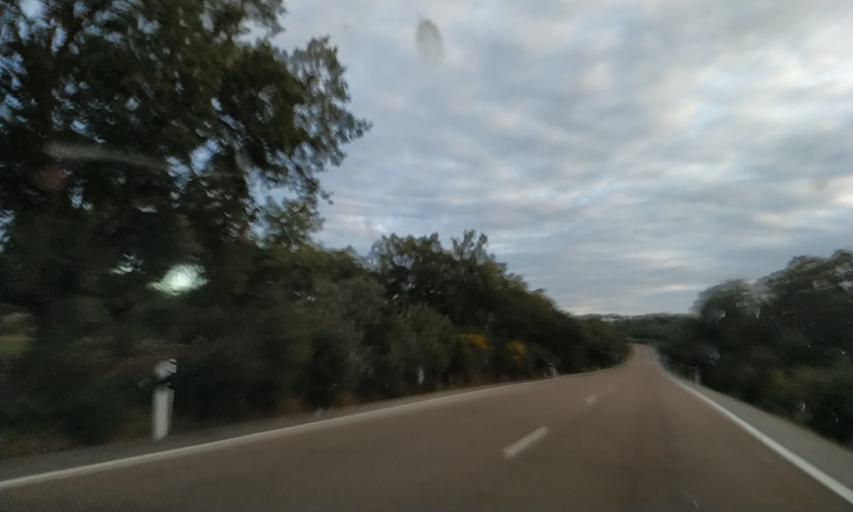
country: ES
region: Extremadura
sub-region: Provincia de Badajoz
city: Puebla de Obando
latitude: 39.2509
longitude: -6.5566
